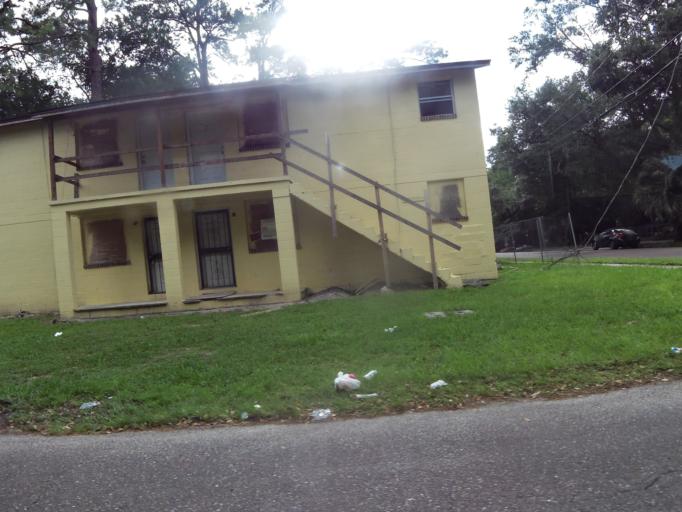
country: US
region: Florida
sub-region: Duval County
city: Jacksonville
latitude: 30.3655
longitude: -81.6814
